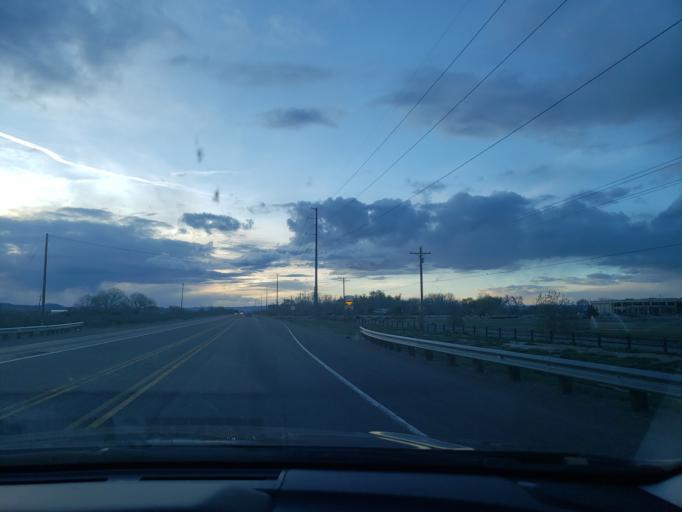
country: US
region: Colorado
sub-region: Mesa County
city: Redlands
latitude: 39.1225
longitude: -108.6689
